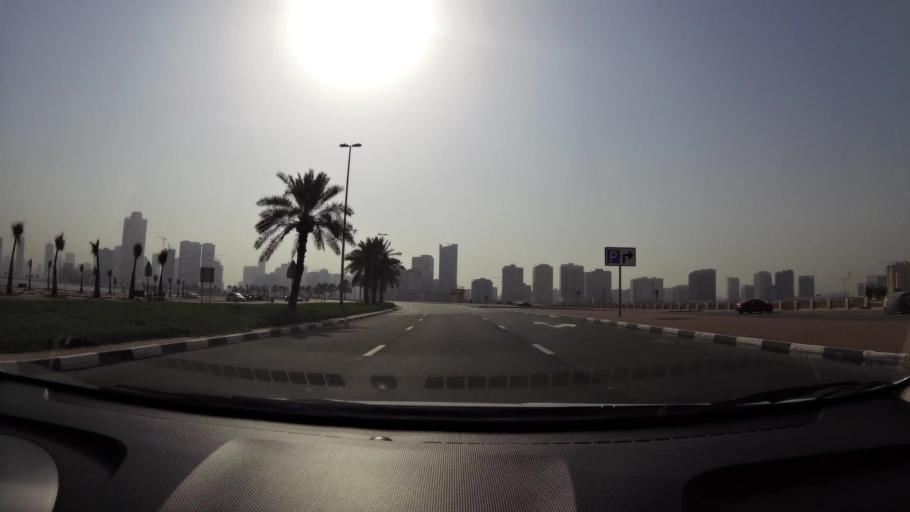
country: AE
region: Ash Shariqah
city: Sharjah
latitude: 25.2973
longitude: 55.3533
